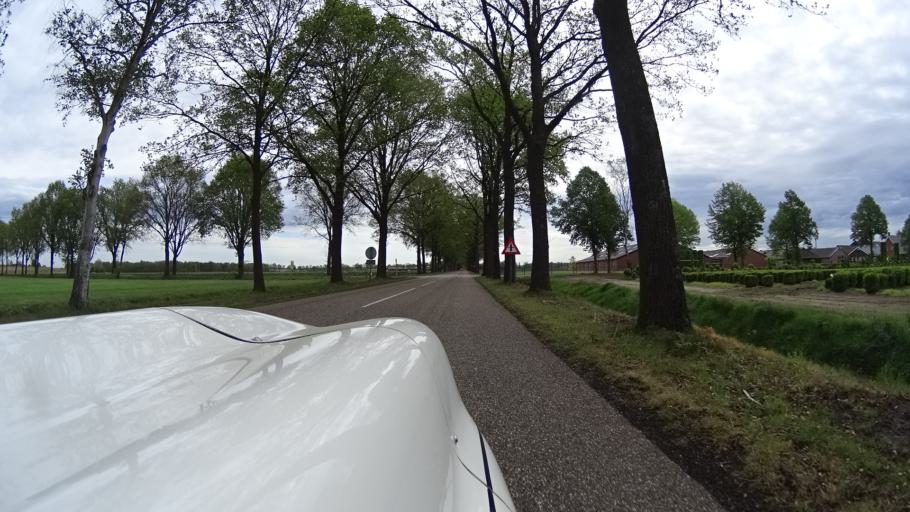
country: NL
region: North Brabant
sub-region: Gemeente Boekel
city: Boekel
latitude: 51.5467
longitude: 5.7278
